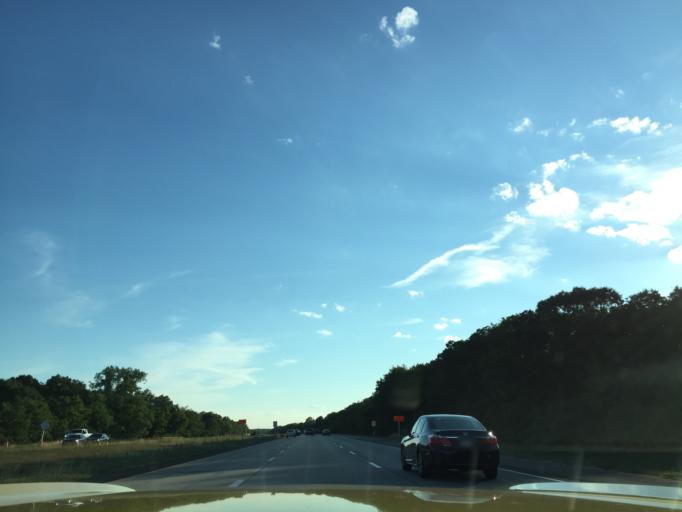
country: US
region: New York
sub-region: Suffolk County
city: Manorville
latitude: 40.8627
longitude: -72.8248
